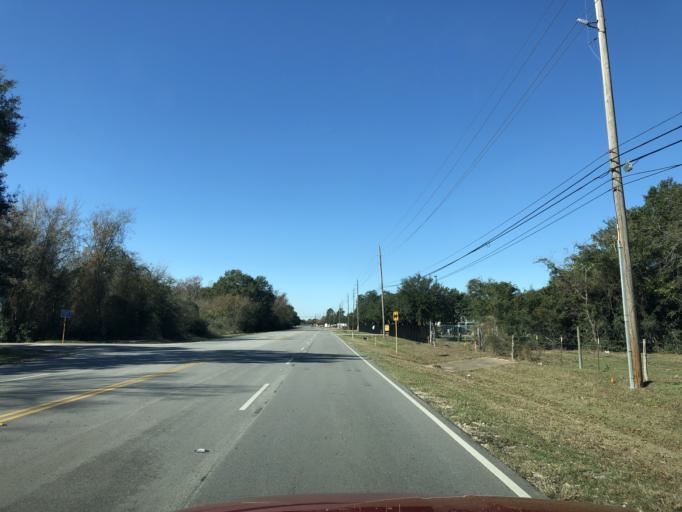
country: US
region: Texas
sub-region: Harris County
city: Oak Cliff Place
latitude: 29.9457
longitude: -95.6544
